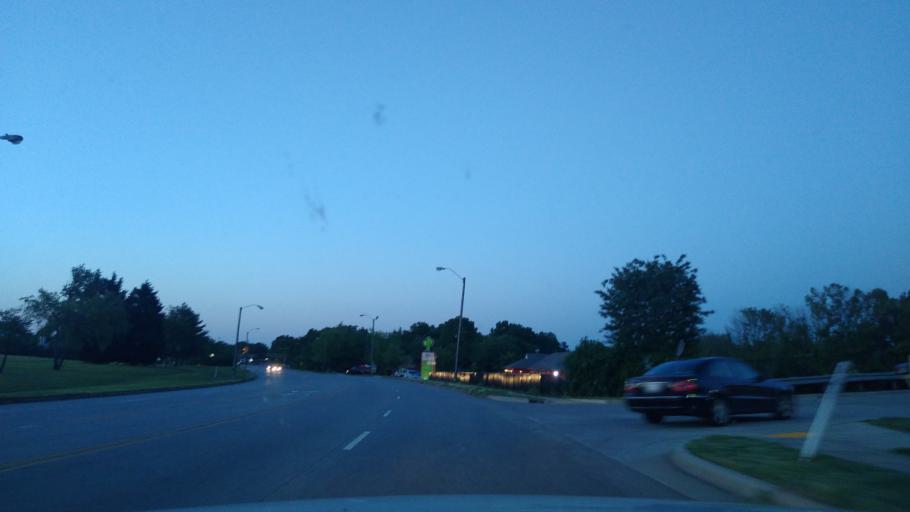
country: US
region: North Carolina
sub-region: Guilford County
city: Jamestown
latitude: 36.0815
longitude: -79.9309
